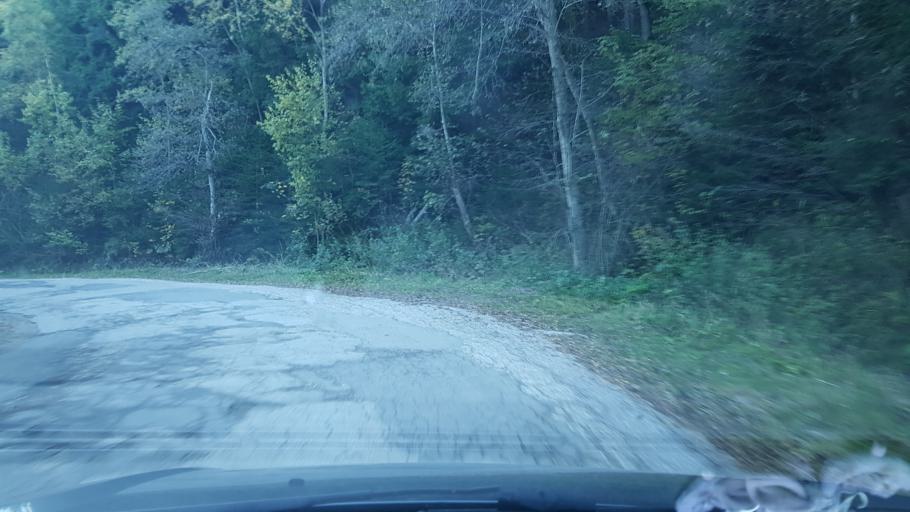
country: SI
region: Slovenj Gradec
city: Legen
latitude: 46.4897
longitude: 15.1784
